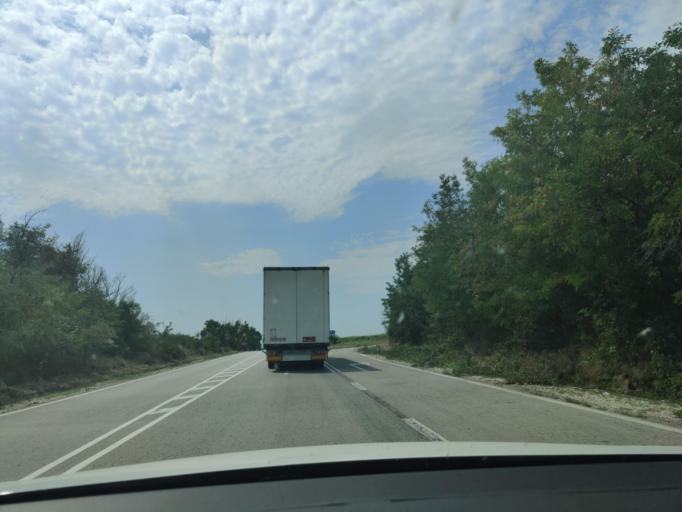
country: BG
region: Vidin
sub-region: Obshtina Vidin
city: Dunavtsi
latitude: 43.8650
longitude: 22.7823
